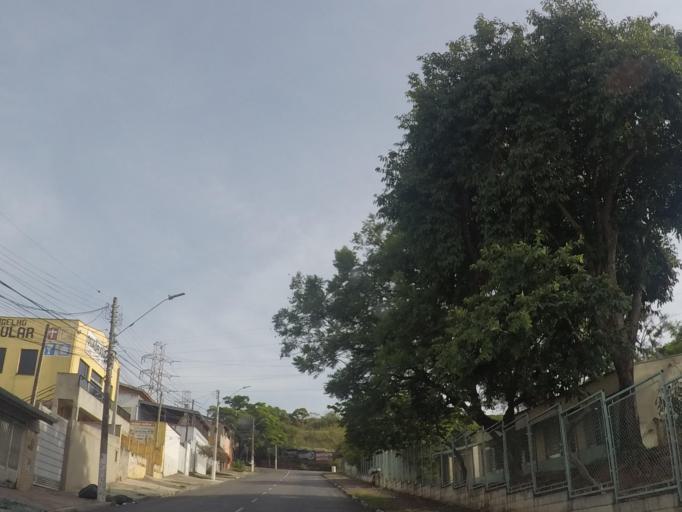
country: BR
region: Sao Paulo
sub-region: Hortolandia
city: Hortolandia
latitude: -22.8639
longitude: -47.1998
